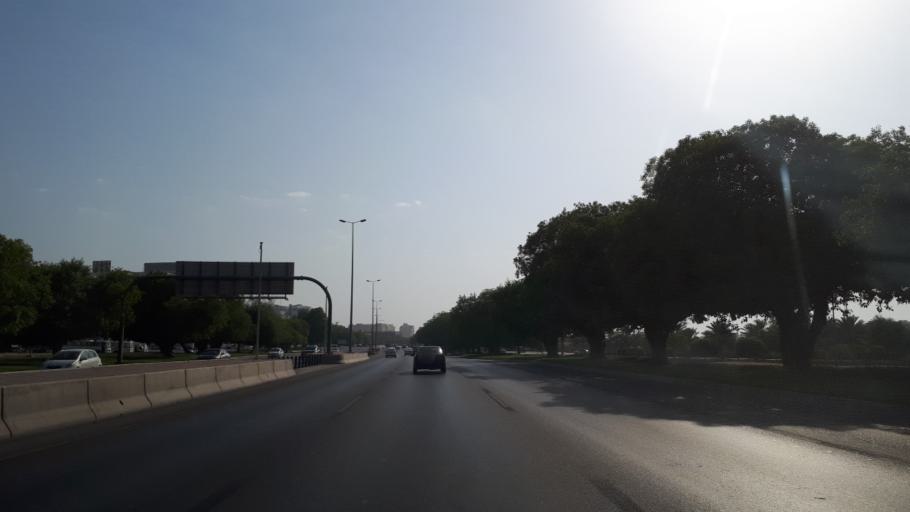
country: OM
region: Muhafazat Masqat
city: Bawshar
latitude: 23.5907
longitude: 58.3701
